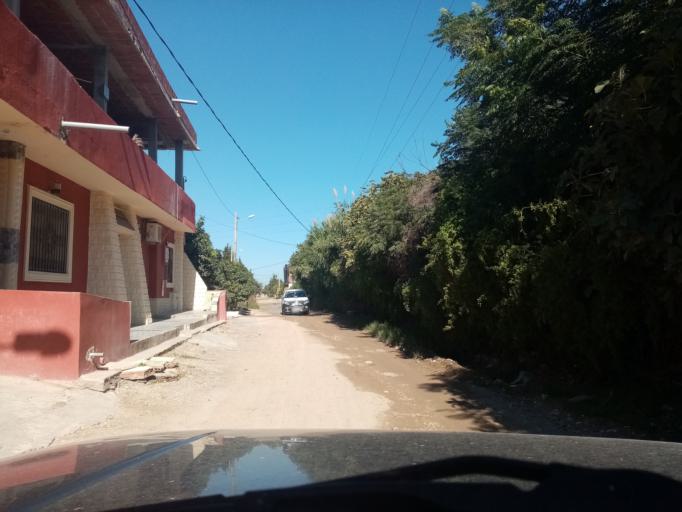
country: TN
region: Nabul
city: Bu `Urqub
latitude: 36.5748
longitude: 10.5729
